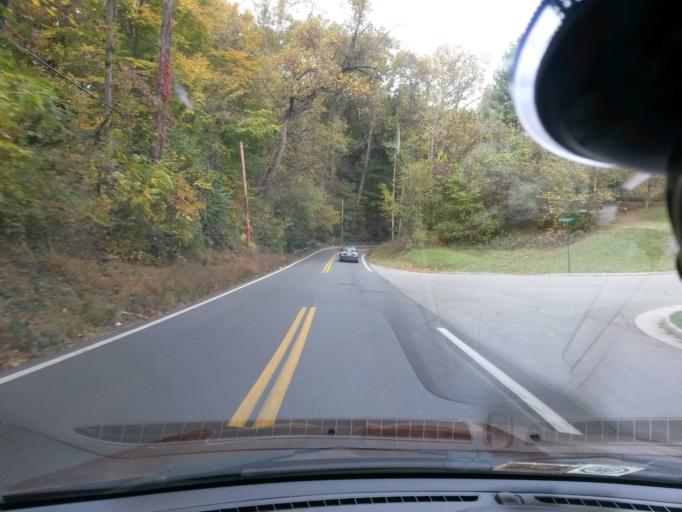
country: US
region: Virginia
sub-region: City of Roanoke
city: Cedar Bluff
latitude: 37.2467
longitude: -79.9127
